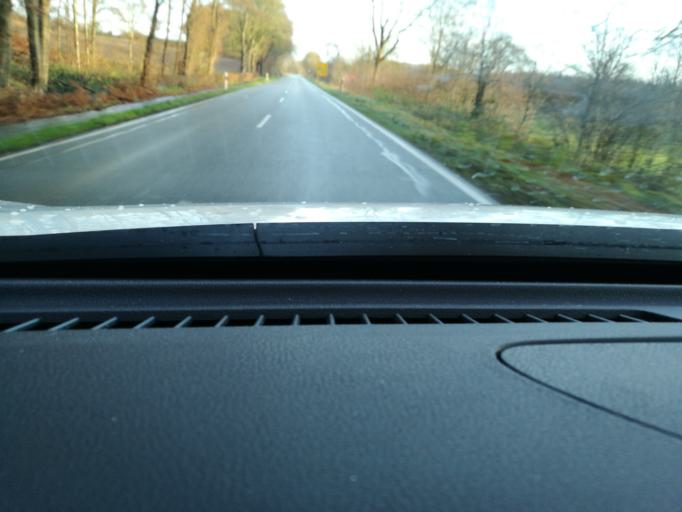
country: DE
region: Schleswig-Holstein
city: Ascheffel
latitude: 54.4110
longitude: 9.6965
